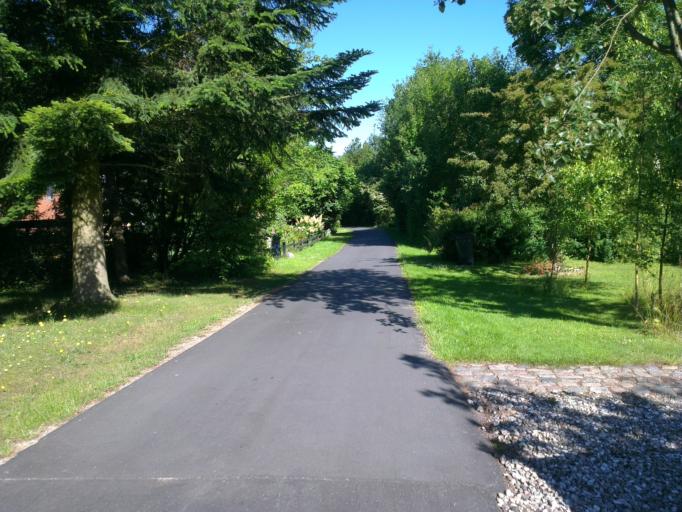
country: DK
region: Capital Region
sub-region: Halsnaes Kommune
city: Hundested
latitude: 55.9166
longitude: 11.9083
